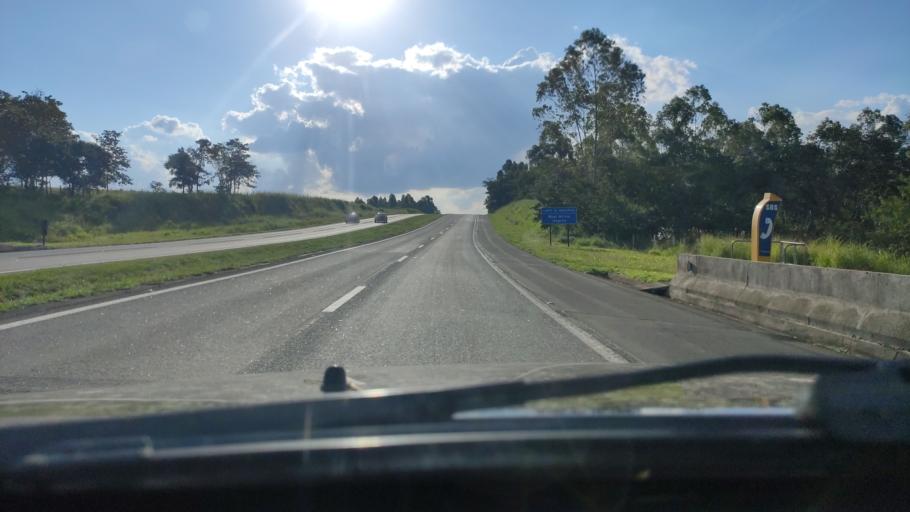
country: BR
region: Sao Paulo
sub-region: Itapira
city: Itapira
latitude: -22.4523
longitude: -46.8738
